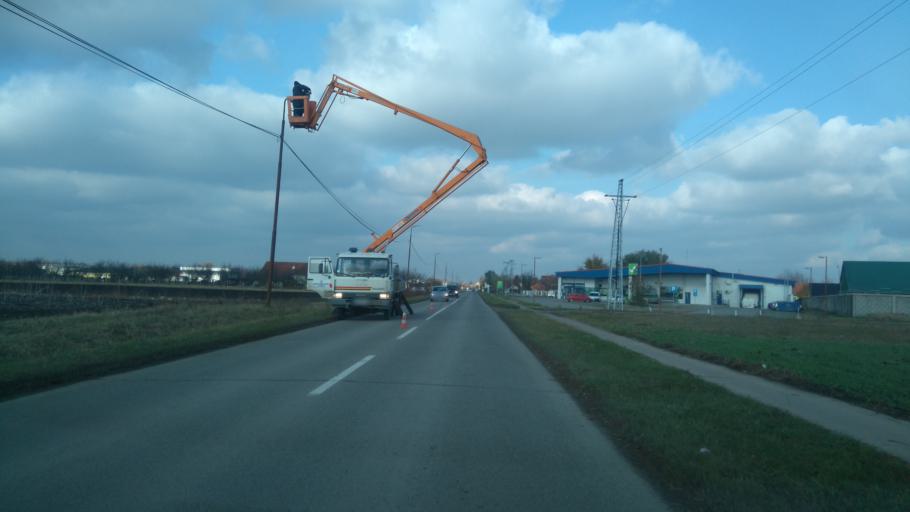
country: RS
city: Mol
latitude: 45.7804
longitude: 20.1280
